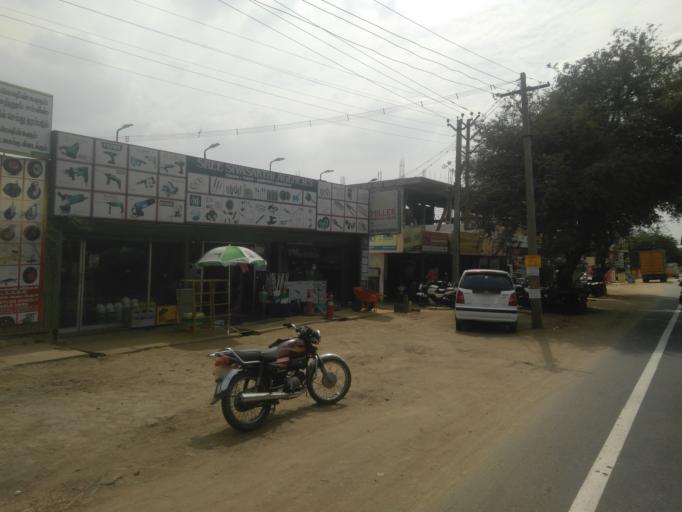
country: IN
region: Tamil Nadu
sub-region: Coimbatore
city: Irugur
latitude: 11.0105
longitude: 77.0812
